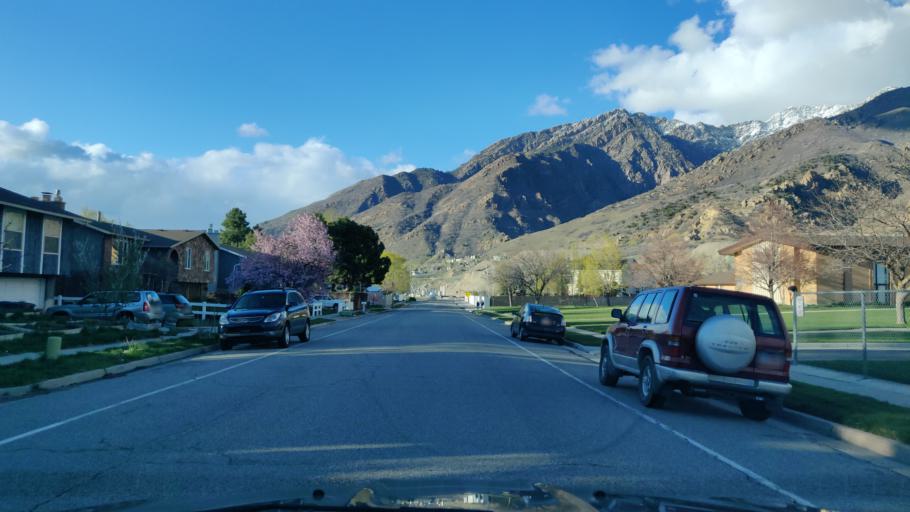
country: US
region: Utah
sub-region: Salt Lake County
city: Cottonwood Heights
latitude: 40.6203
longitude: -111.8002
